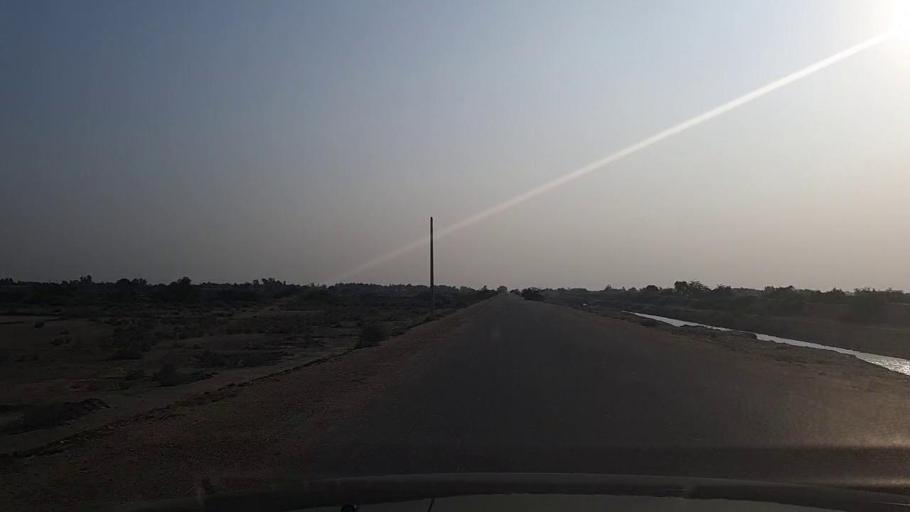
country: PK
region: Sindh
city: Mirpur Sakro
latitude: 24.5088
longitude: 67.8178
